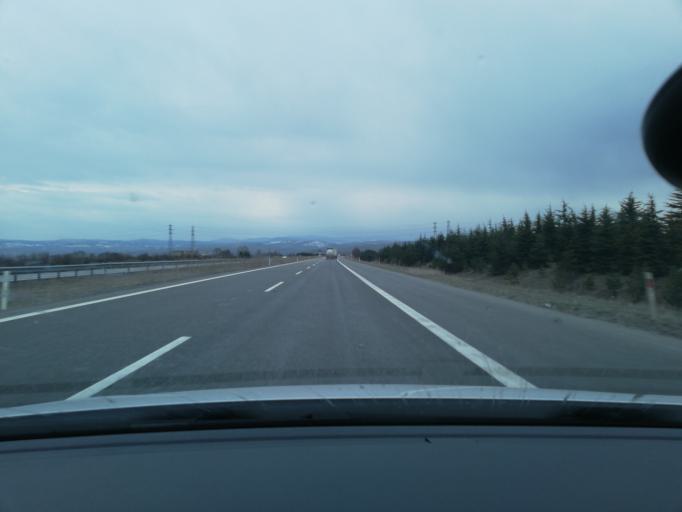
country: TR
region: Bolu
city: Gerede
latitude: 40.7655
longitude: 32.2040
